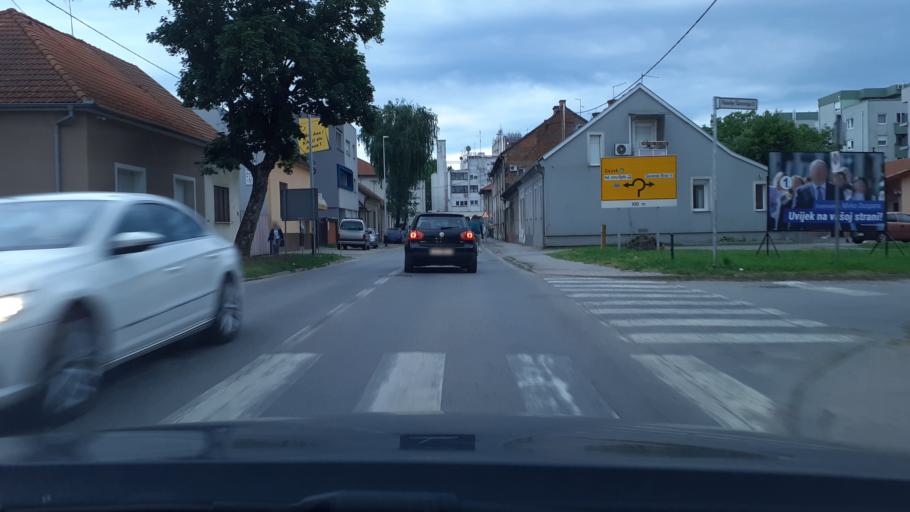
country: HR
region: Brodsko-Posavska
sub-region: Grad Slavonski Brod
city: Slavonski Brod
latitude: 45.1601
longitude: 18.0235
